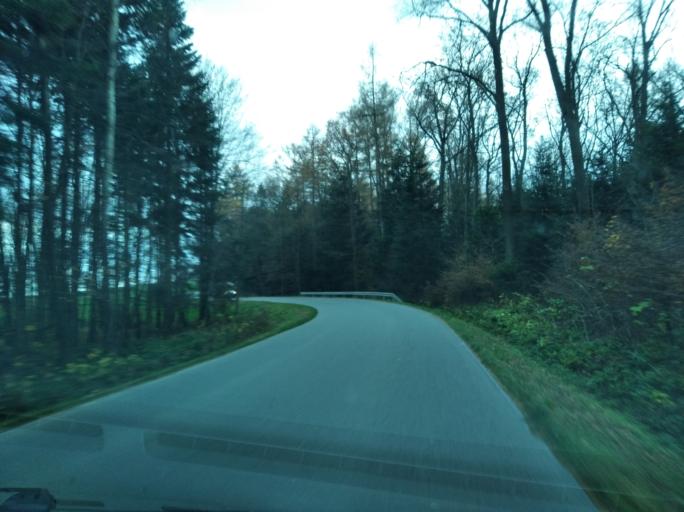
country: PL
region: Subcarpathian Voivodeship
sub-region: Powiat ropczycko-sedziszowski
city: Zagorzyce
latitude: 49.9600
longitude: 21.6927
